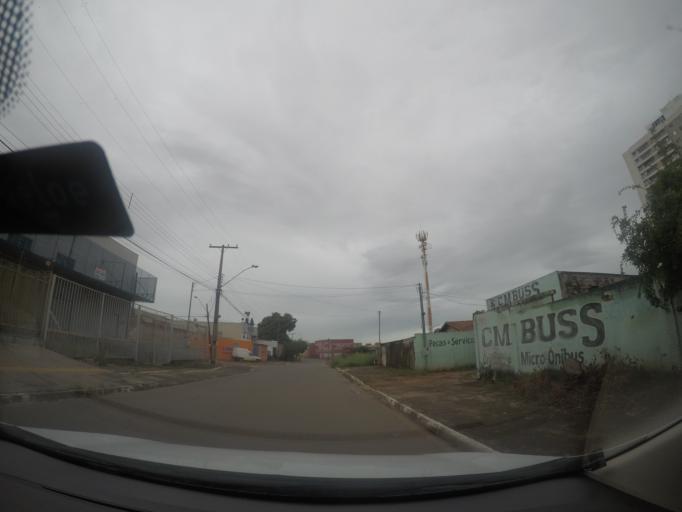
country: BR
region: Goias
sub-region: Goiania
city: Goiania
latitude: -16.6678
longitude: -49.3212
